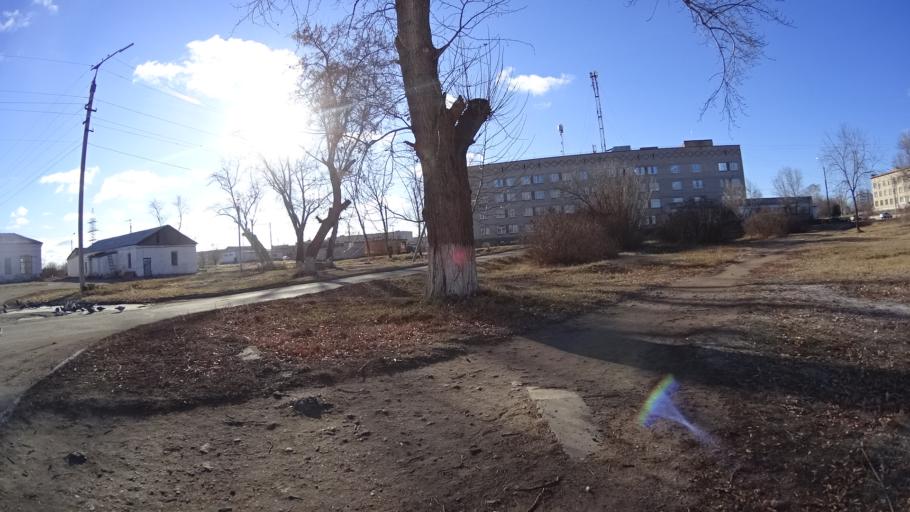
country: RU
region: Chelyabinsk
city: Troitsk
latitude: 54.0764
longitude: 61.5352
